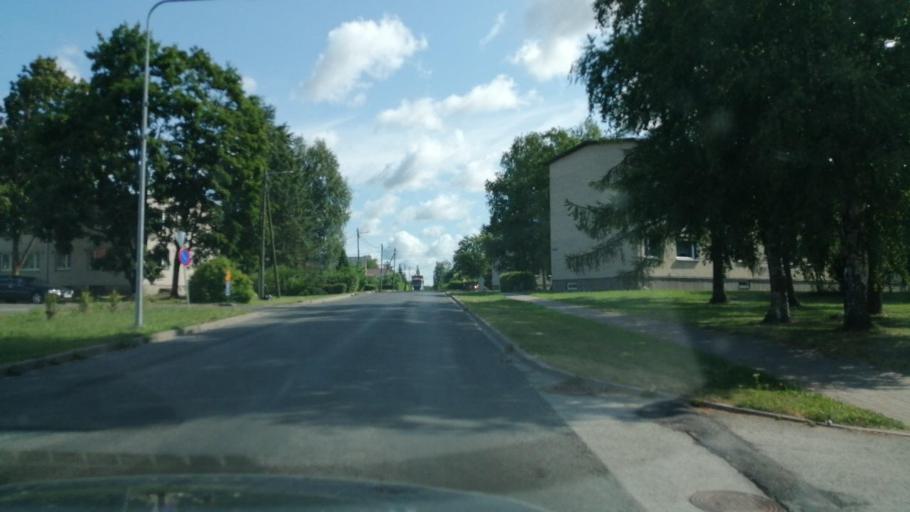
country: EE
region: Viljandimaa
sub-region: Viiratsi vald
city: Viiratsi
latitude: 58.3592
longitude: 25.6406
